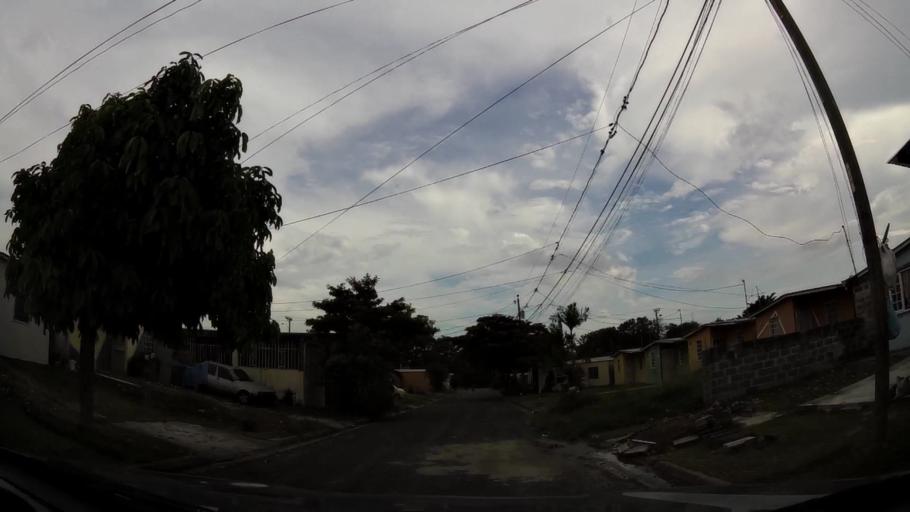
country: PA
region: Panama
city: Cabra Numero Uno
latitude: 9.0879
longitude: -79.3448
